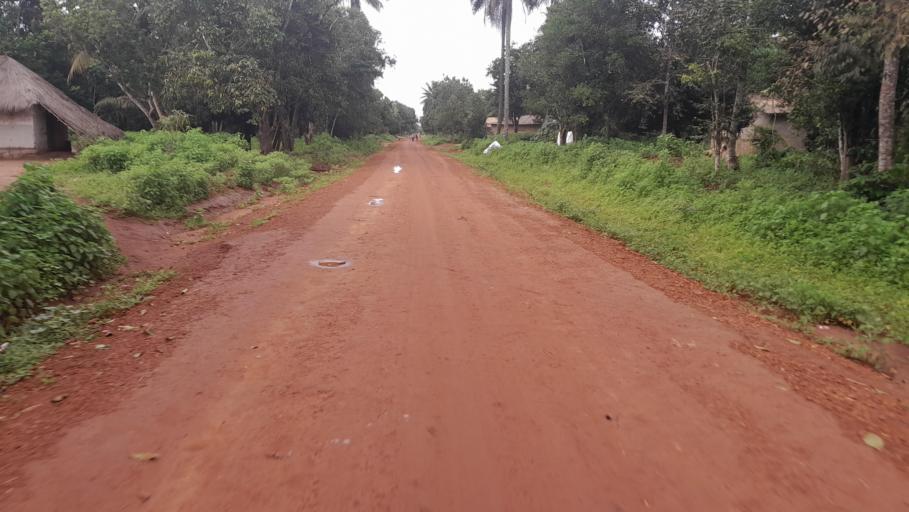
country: GN
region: Boke
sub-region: Boffa
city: Boffa
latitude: 10.0125
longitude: -13.8876
